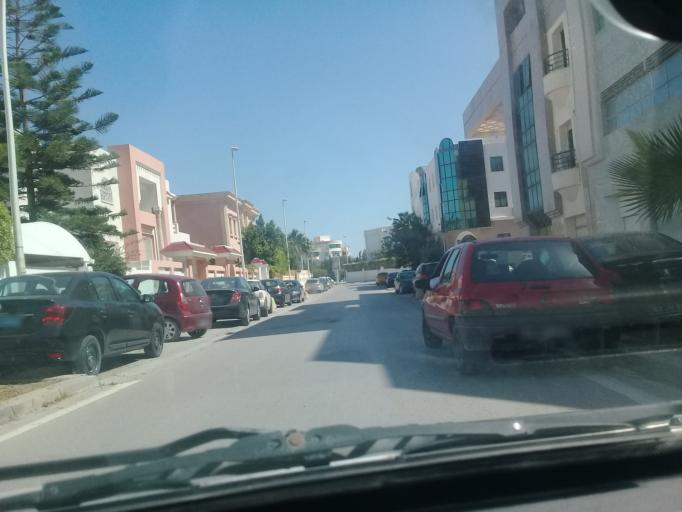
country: TN
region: Ariana
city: Ariana
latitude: 36.8399
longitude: 10.2458
